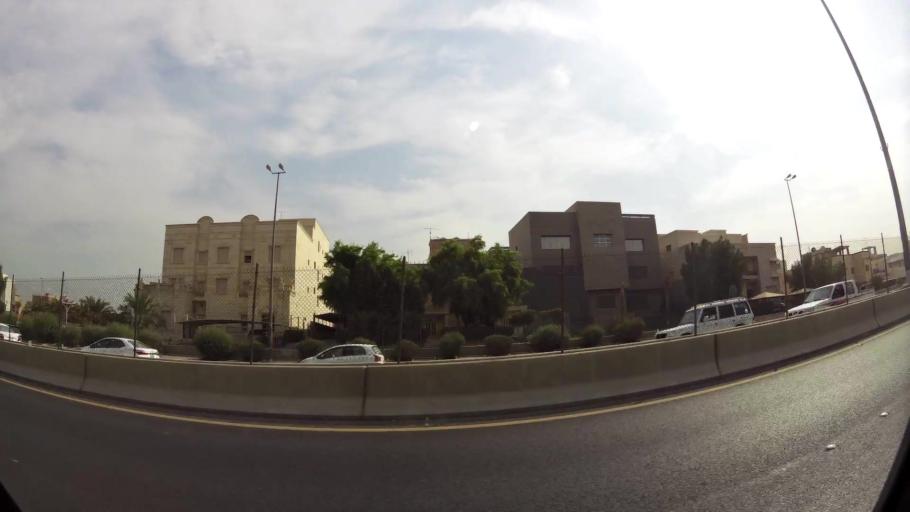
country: KW
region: Al Asimah
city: Ash Shamiyah
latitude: 29.3347
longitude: 47.9713
